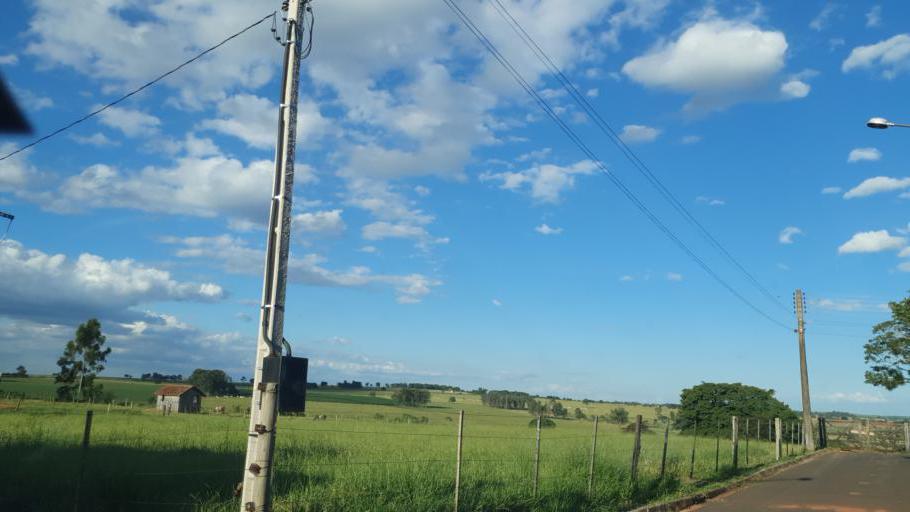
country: BR
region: Sao Paulo
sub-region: Quata
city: Quata
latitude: -22.2504
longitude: -50.7655
